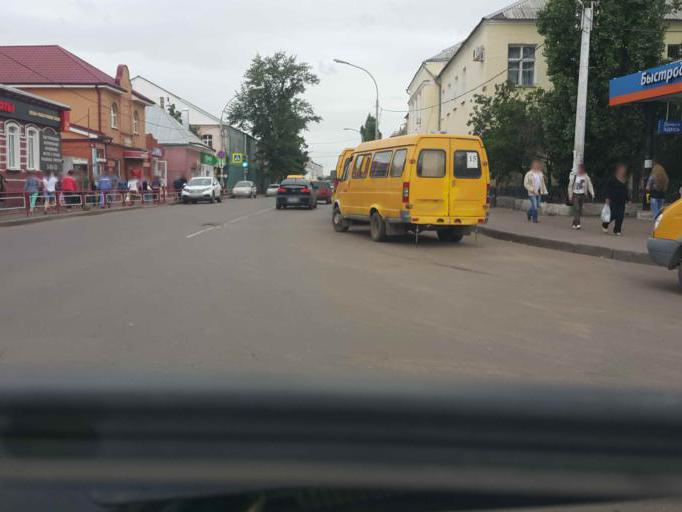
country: RU
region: Tambov
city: Michurinsk
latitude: 52.8870
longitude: 40.5127
